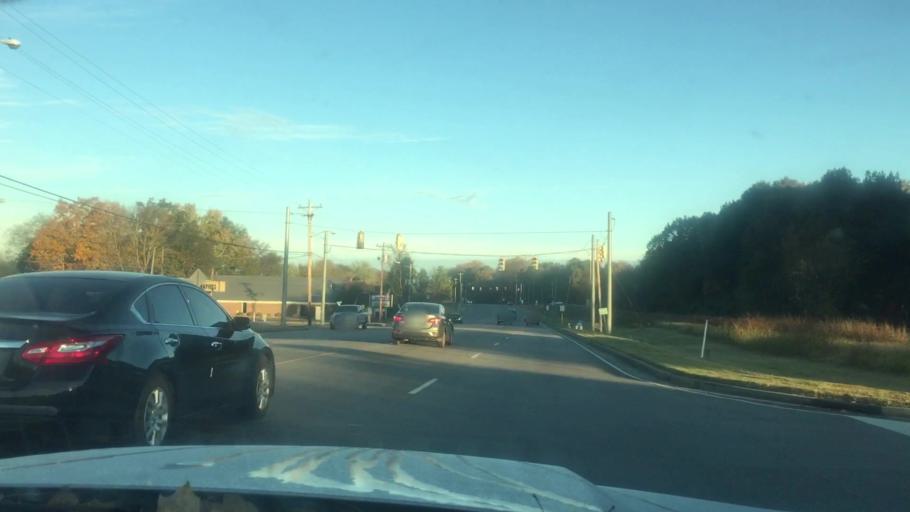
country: US
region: Tennessee
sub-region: Franklin County
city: Estill Springs
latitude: 35.2706
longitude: -86.1279
